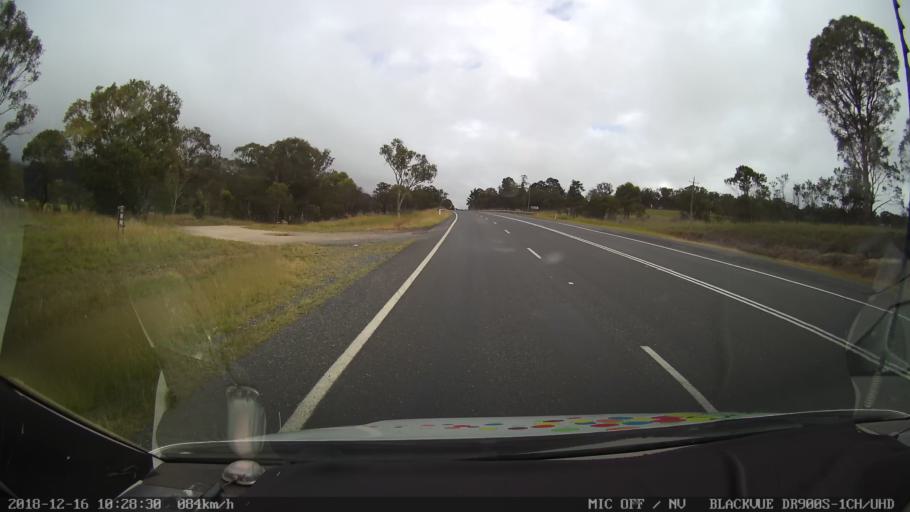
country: AU
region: New South Wales
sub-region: Tenterfield Municipality
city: Carrolls Creek
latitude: -29.1205
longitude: 151.9971
